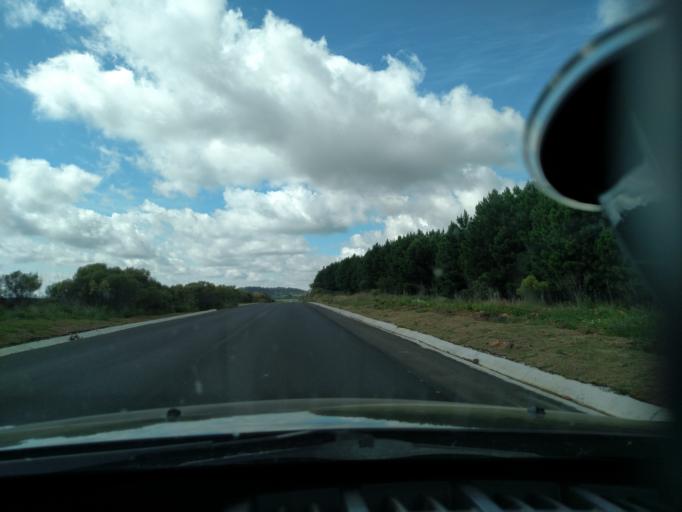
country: BR
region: Santa Catarina
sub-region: Sao Joaquim
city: Sao Joaquim
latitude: -28.0284
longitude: -50.0784
